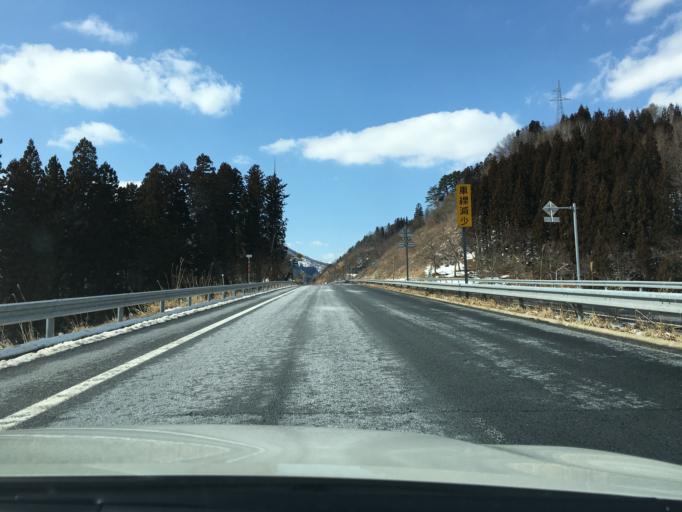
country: JP
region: Yamagata
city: Sagae
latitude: 38.4380
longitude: 140.0812
